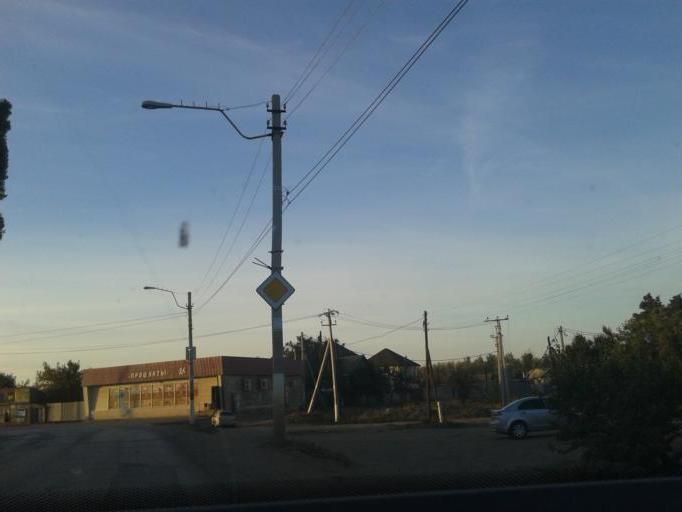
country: RU
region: Volgograd
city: Krasnoslobodsk
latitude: 48.7084
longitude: 44.5797
